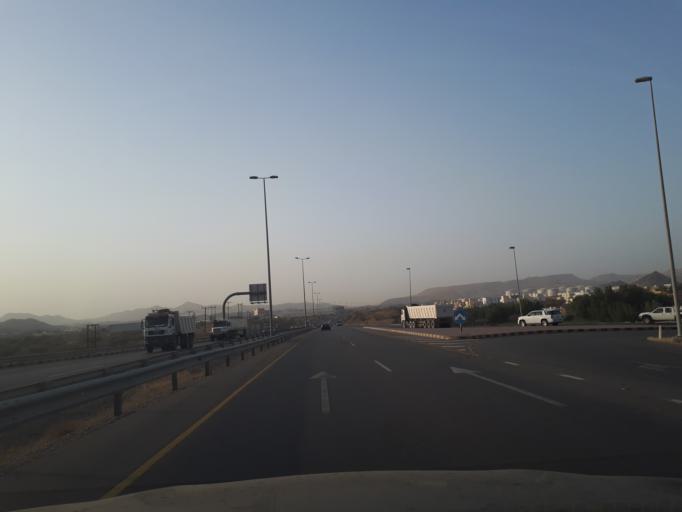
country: OM
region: Muhafazat ad Dakhiliyah
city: Bidbid
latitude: 23.4865
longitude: 58.1972
